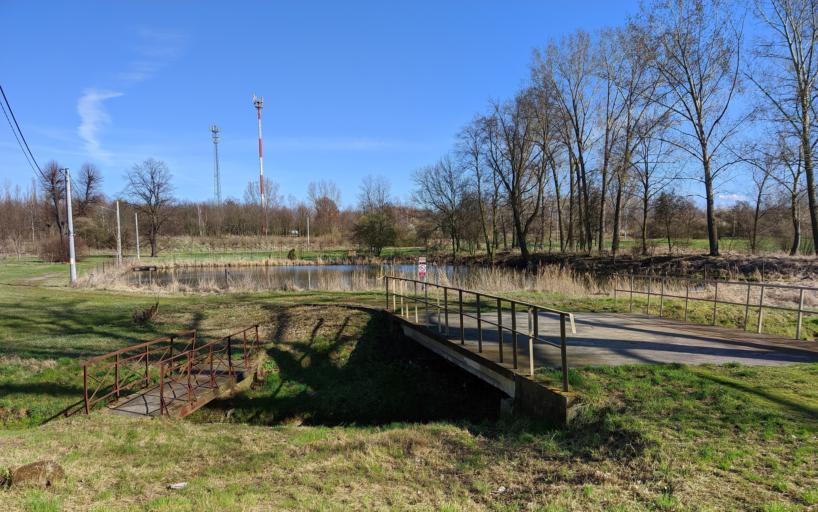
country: PL
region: Lower Silesian Voivodeship
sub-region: Powiat glogowski
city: Kotla
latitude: 51.6745
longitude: 15.9816
